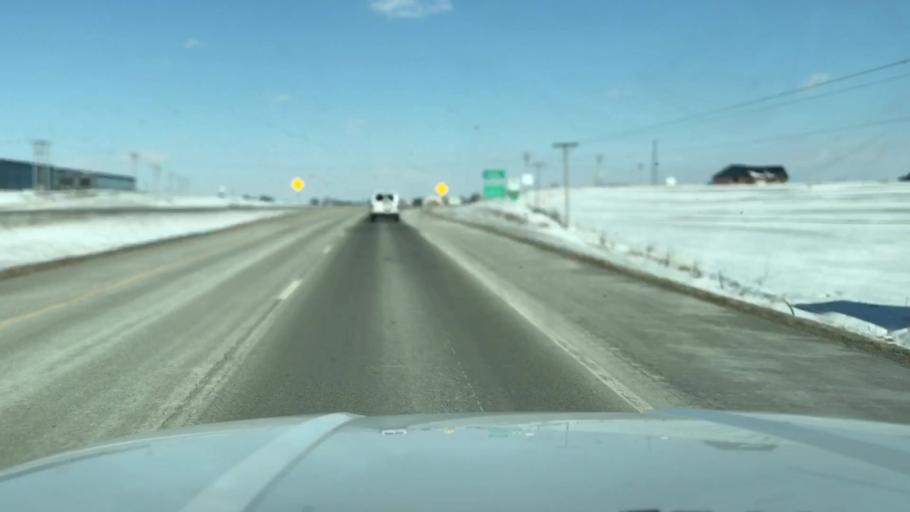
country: US
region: Missouri
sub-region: Nodaway County
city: Maryville
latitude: 40.3092
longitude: -94.8742
